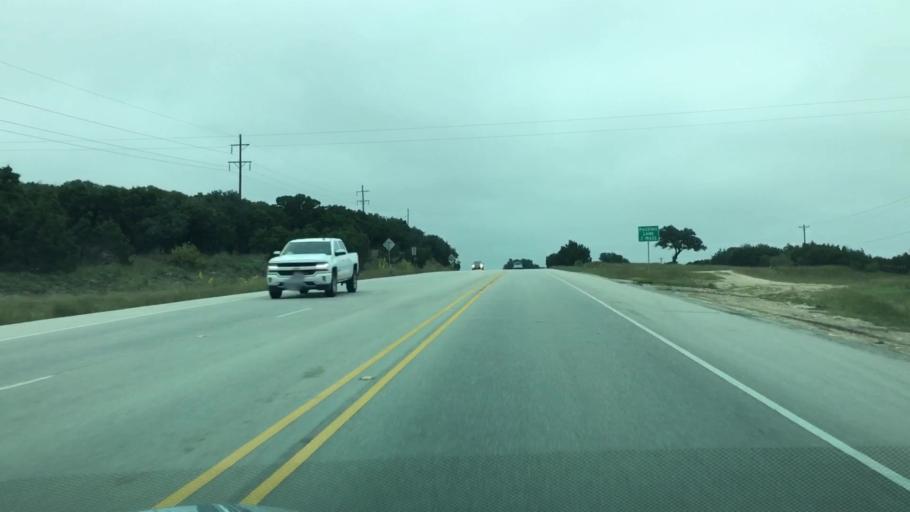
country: US
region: Texas
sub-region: Blanco County
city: Blanco
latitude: 29.9786
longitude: -98.4099
